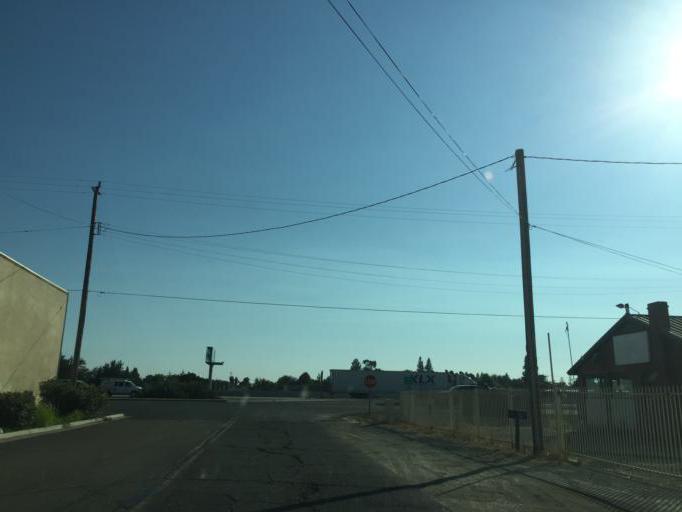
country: US
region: California
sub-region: Fresno County
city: Kingsburg
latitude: 36.5098
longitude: -119.5505
